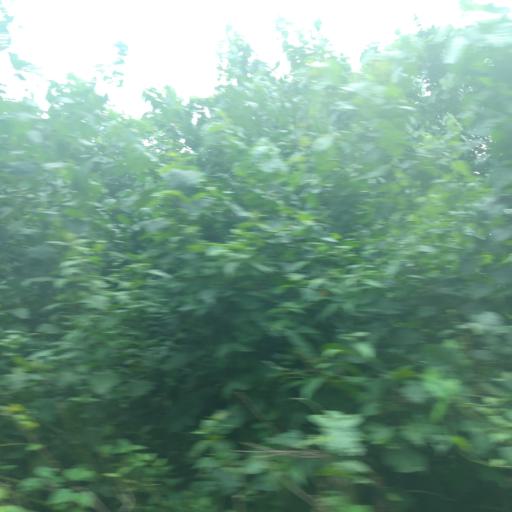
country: NG
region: Ogun
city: Odogbolu
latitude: 6.6637
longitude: 3.7105
